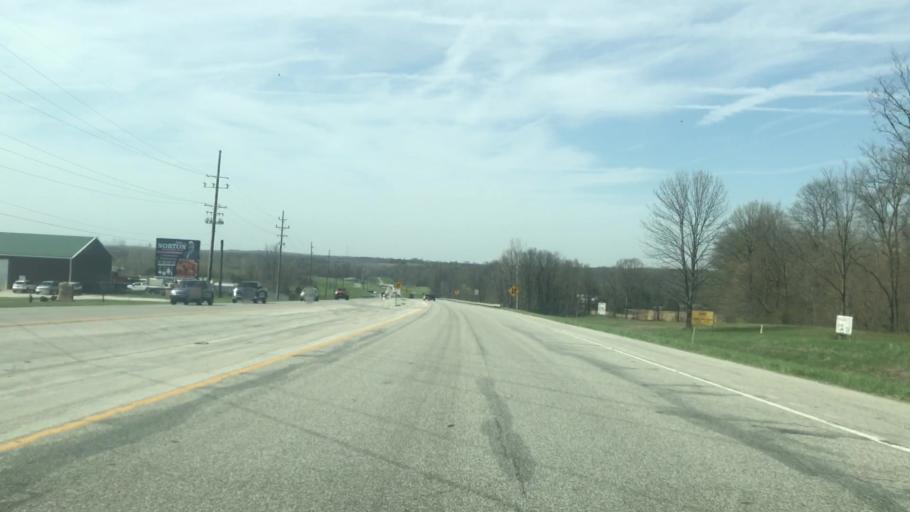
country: US
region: Indiana
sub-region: Putnam County
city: Cloverdale
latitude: 39.5384
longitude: -86.8039
